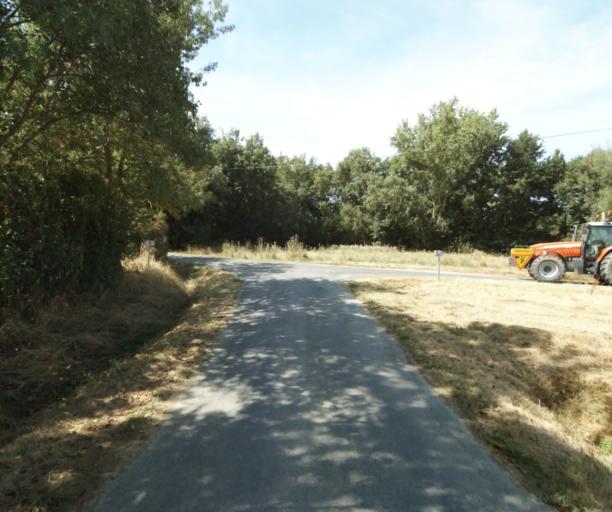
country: FR
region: Midi-Pyrenees
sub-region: Departement du Tarn
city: Puylaurens
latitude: 43.5150
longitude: 2.0292
